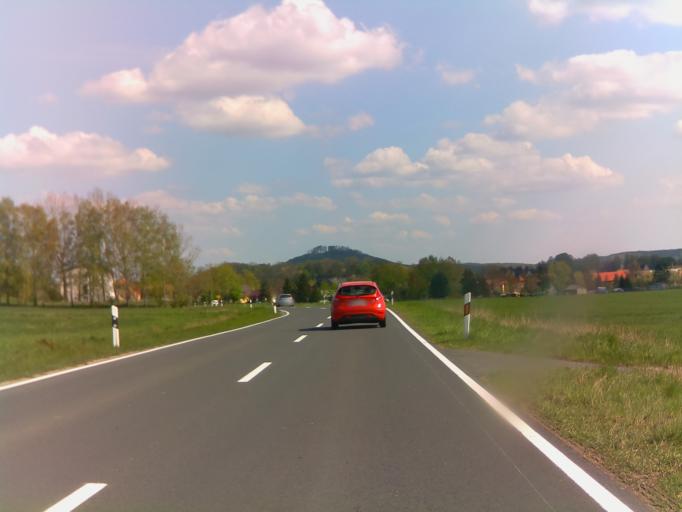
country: DE
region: Thuringia
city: Westhausen
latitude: 50.3606
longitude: 10.6773
